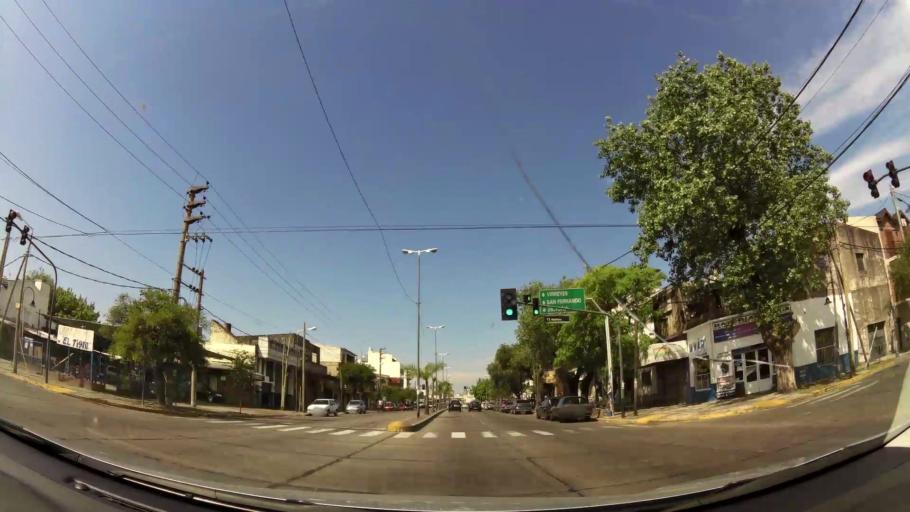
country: AR
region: Buenos Aires
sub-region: Partido de Tigre
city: Tigre
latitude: -34.4618
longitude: -58.5750
